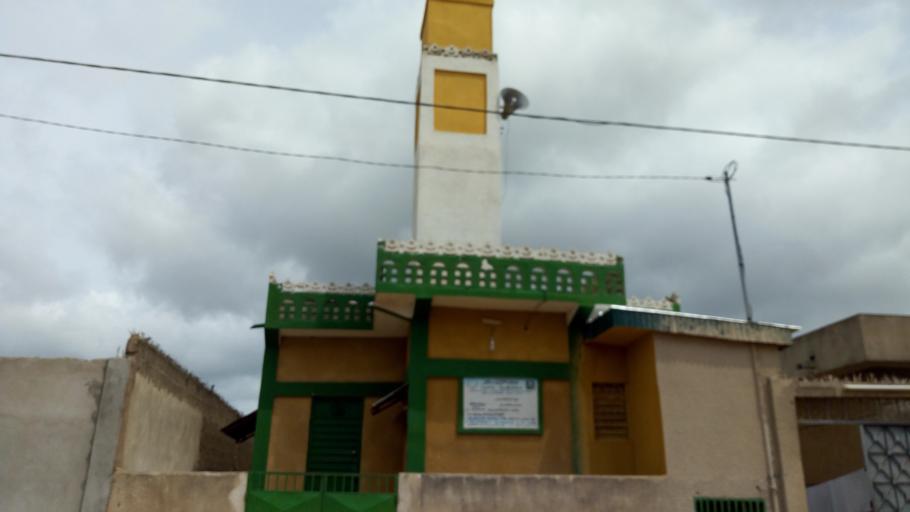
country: CI
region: Vallee du Bandama
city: Bouake
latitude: 7.7252
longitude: -5.0505
